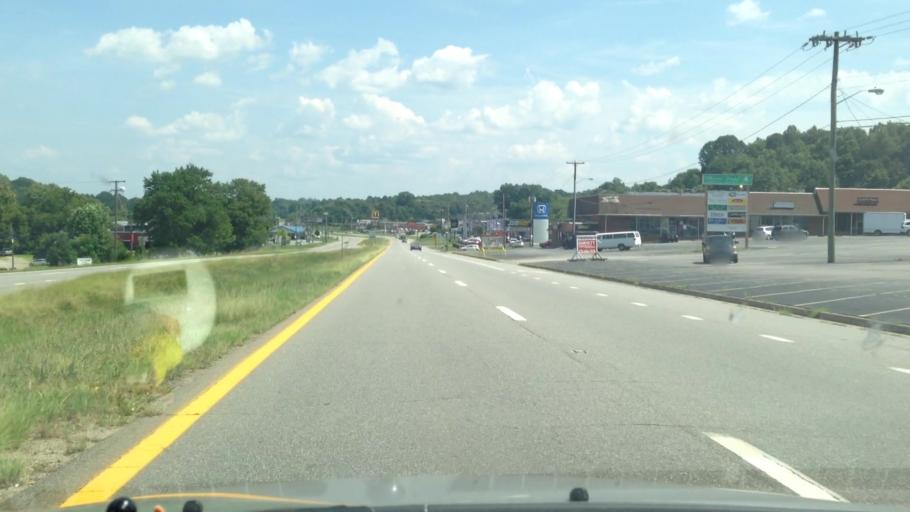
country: US
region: Virginia
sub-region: City of Martinsville
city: Martinsville
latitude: 36.6576
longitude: -79.8794
